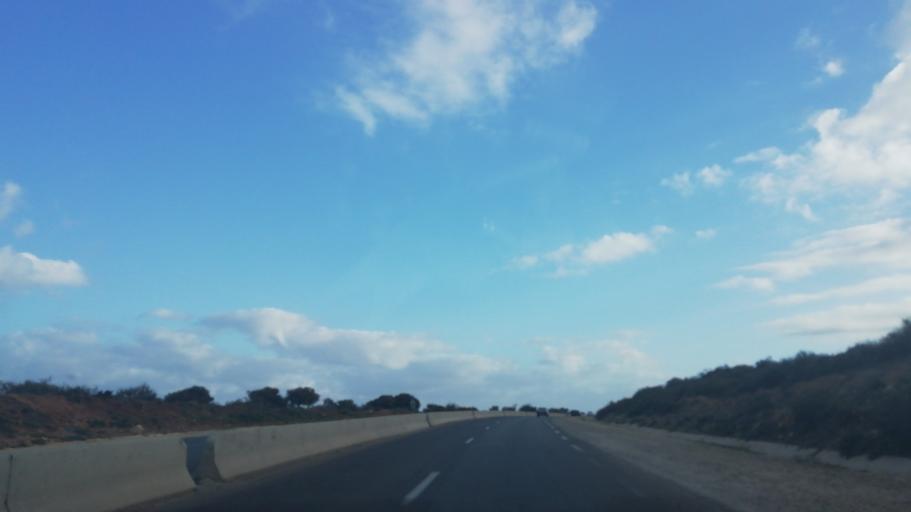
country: DZ
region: Mostaganem
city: Mostaganem
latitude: 36.0857
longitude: 0.1959
